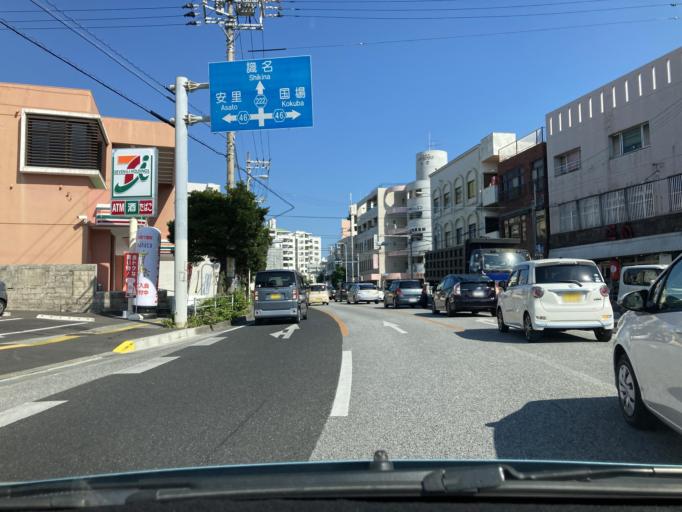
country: JP
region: Okinawa
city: Naha-shi
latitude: 26.2058
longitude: 127.6985
